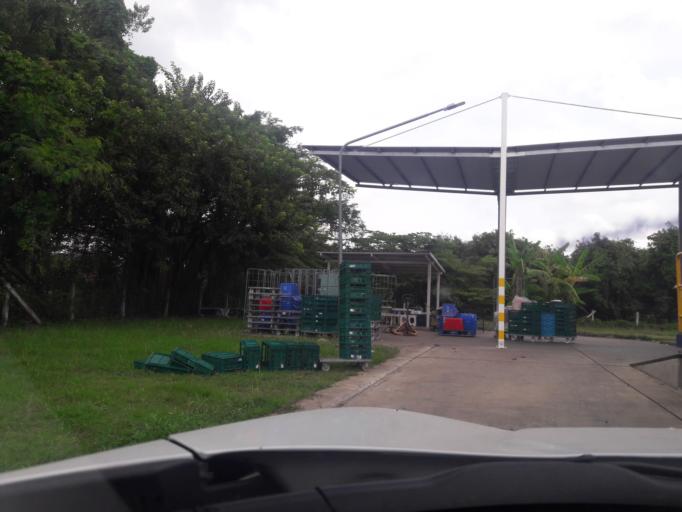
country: TH
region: Lop Buri
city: Ban Mi
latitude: 15.0457
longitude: 100.5485
